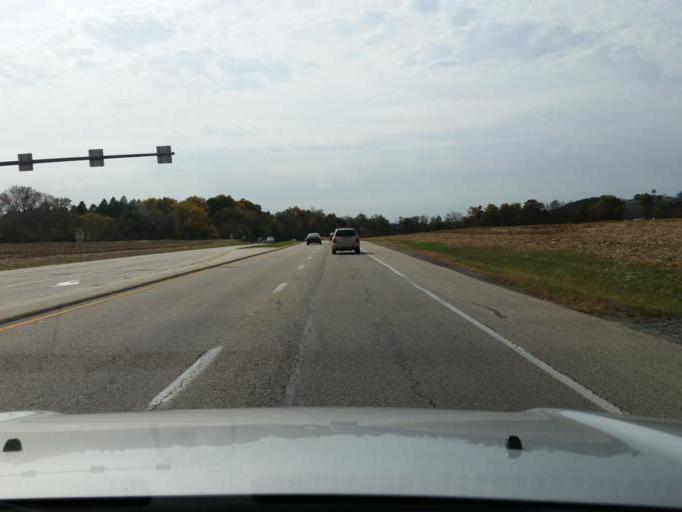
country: US
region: Pennsylvania
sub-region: Dauphin County
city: Palmdale
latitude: 40.3084
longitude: -76.6181
